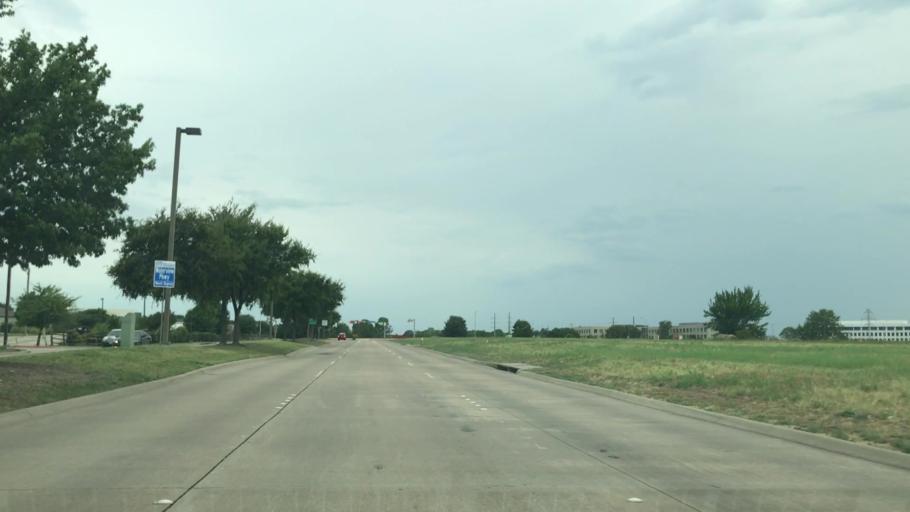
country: US
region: Texas
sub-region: Collin County
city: Plano
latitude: 33.0008
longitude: -96.7452
